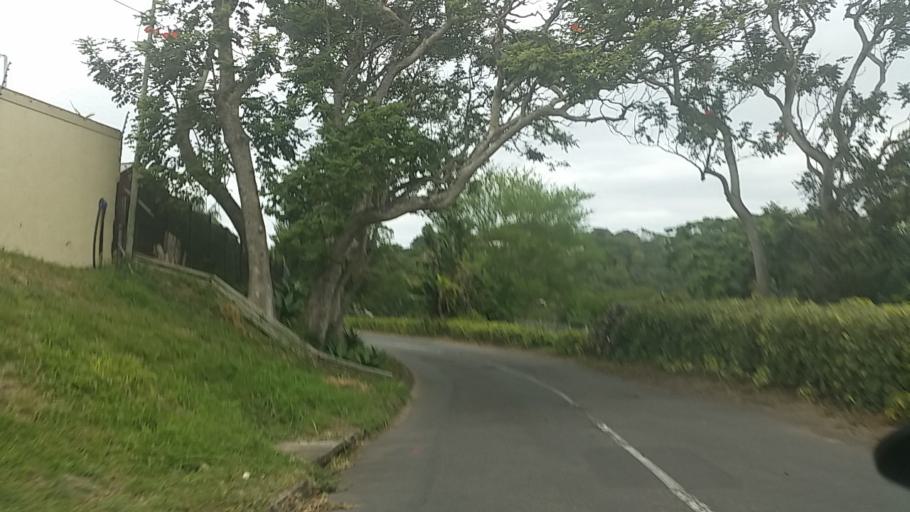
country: ZA
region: KwaZulu-Natal
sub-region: eThekwini Metropolitan Municipality
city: Berea
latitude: -29.8384
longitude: 30.9300
